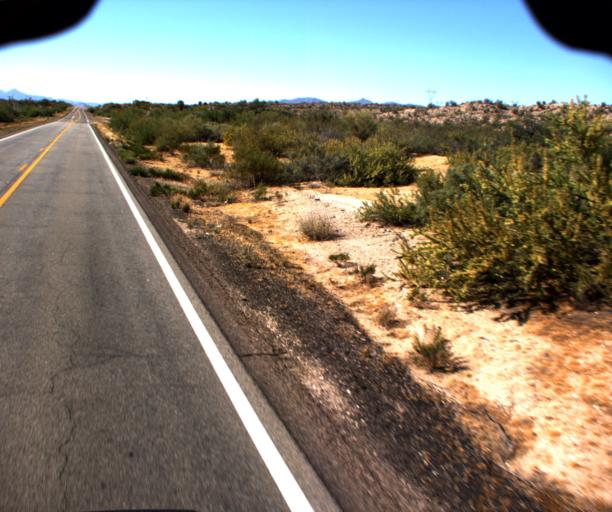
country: US
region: Arizona
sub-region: Yavapai County
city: Bagdad
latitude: 34.7732
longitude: -113.6213
